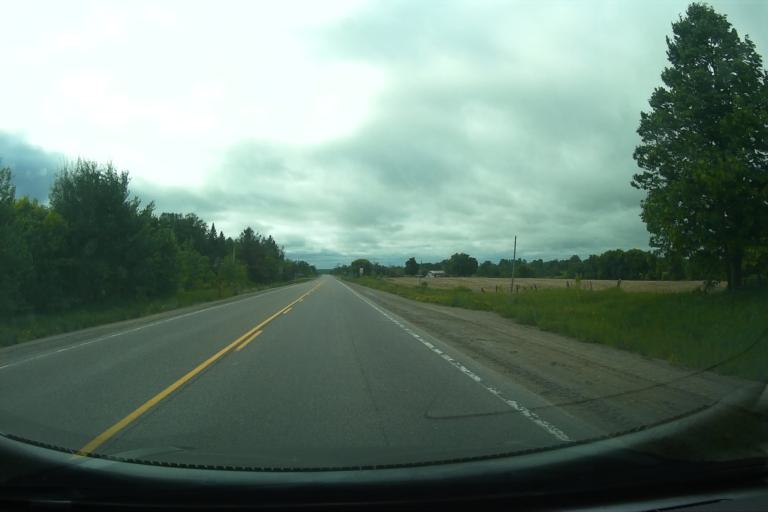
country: CA
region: Ontario
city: Renfrew
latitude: 45.5166
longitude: -76.9483
